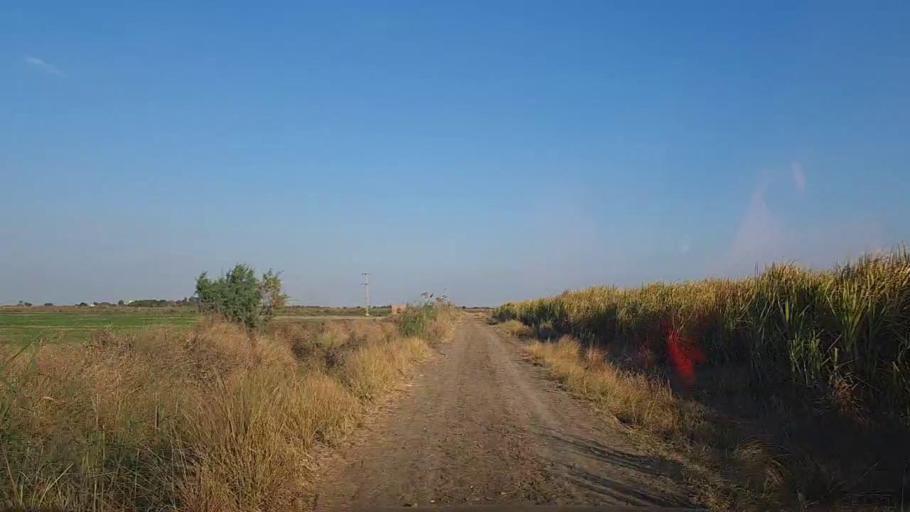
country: PK
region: Sindh
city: Tando Mittha Khan
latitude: 25.9238
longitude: 69.0585
